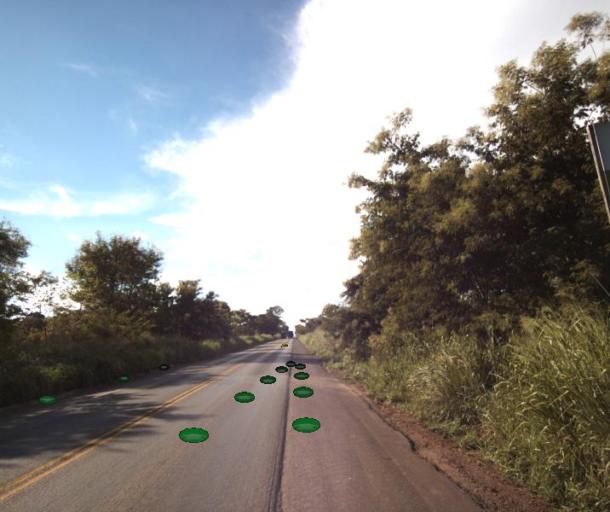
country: BR
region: Goias
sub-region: Rialma
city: Rialma
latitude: -15.3316
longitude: -49.5705
